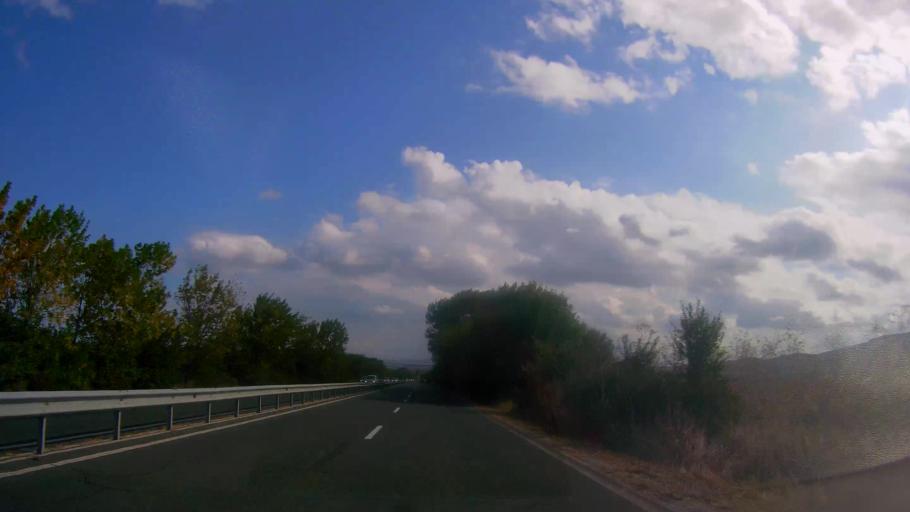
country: BG
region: Burgas
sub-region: Obshtina Sozopol
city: Chernomorets
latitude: 42.4332
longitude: 27.6380
